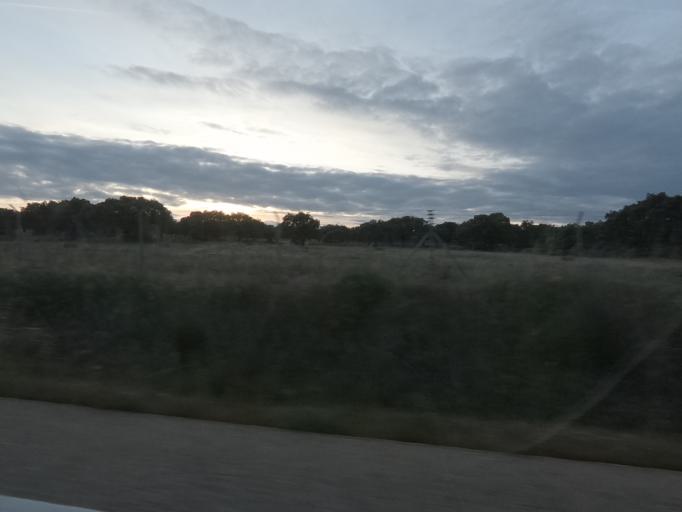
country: ES
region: Extremadura
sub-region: Provincia de Badajoz
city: Villar del Rey
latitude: 39.0090
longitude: -6.8578
